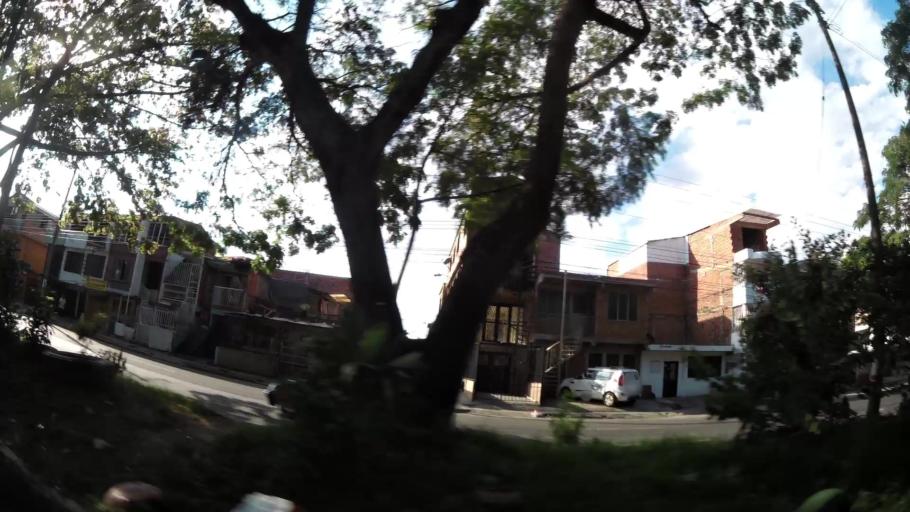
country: CO
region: Valle del Cauca
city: Cali
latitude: 3.4056
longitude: -76.5000
